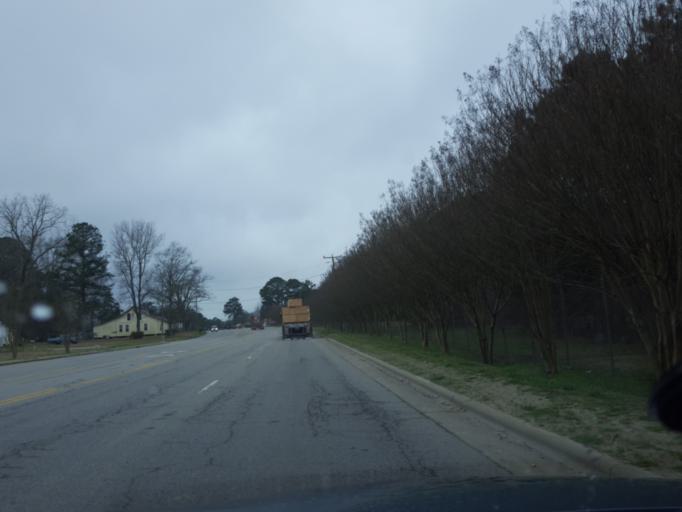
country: US
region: North Carolina
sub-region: Washington County
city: Plymouth
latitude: 35.8333
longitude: -76.7720
